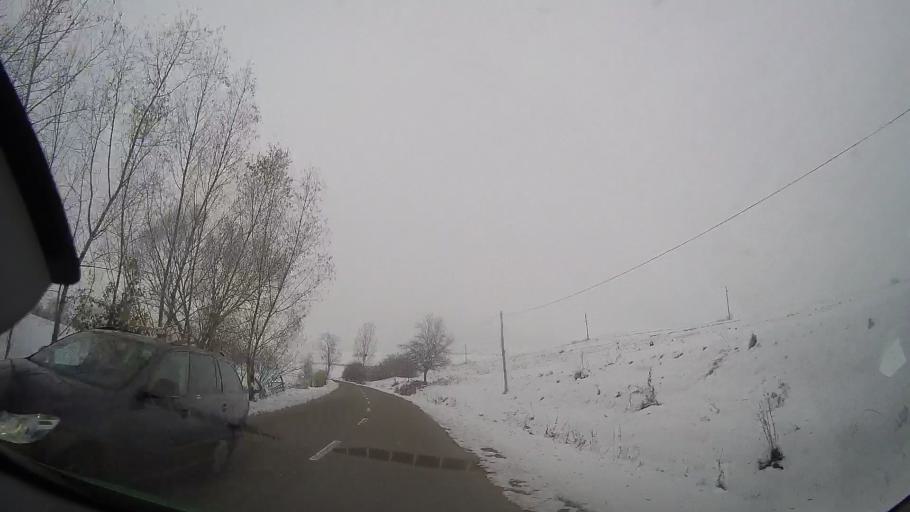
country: RO
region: Neamt
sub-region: Comuna Oniceni
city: Oniceni
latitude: 46.8015
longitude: 27.1366
